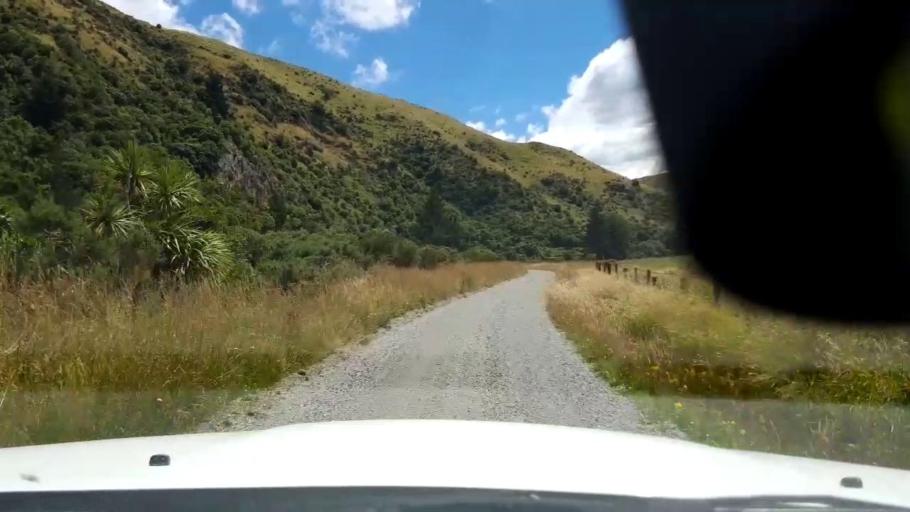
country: NZ
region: Canterbury
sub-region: Timaru District
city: Pleasant Point
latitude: -43.9315
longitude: 171.1937
